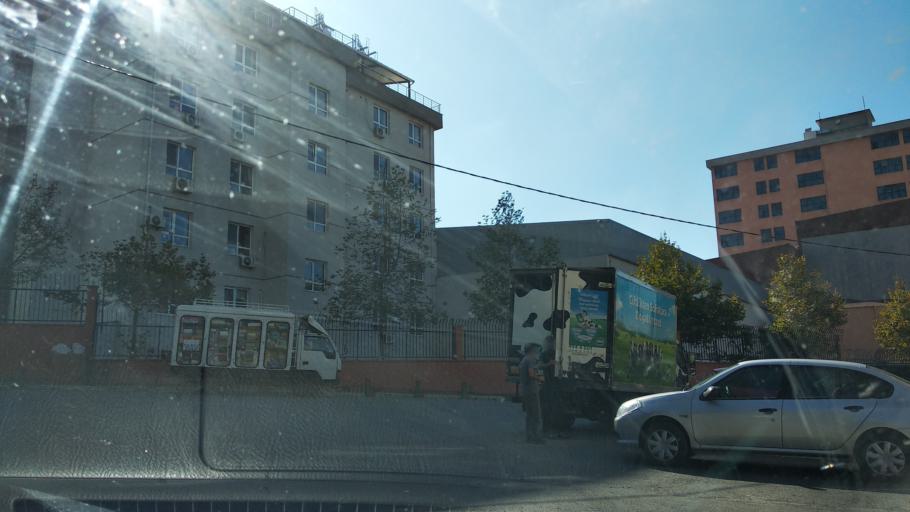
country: TR
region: Istanbul
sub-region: Atasehir
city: Atasehir
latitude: 40.9827
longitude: 29.1091
